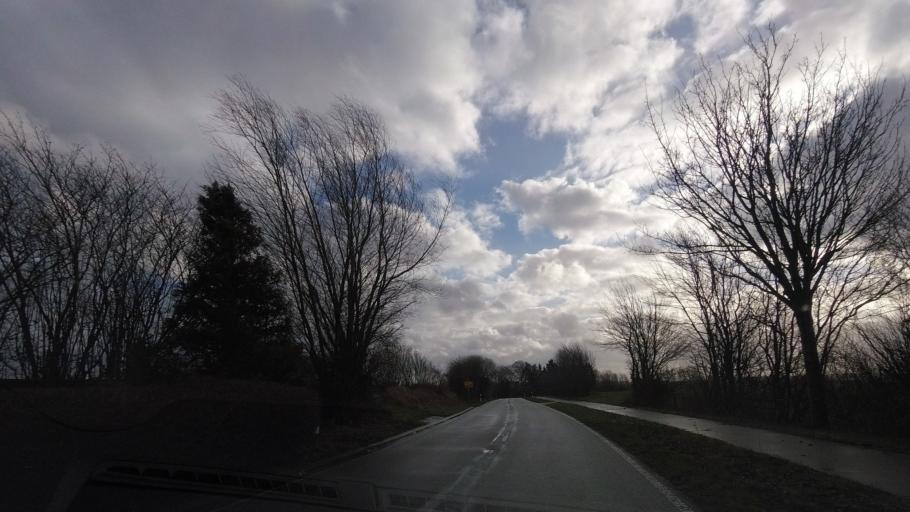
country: DE
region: Schleswig-Holstein
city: Grodersby
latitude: 54.6359
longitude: 9.9210
